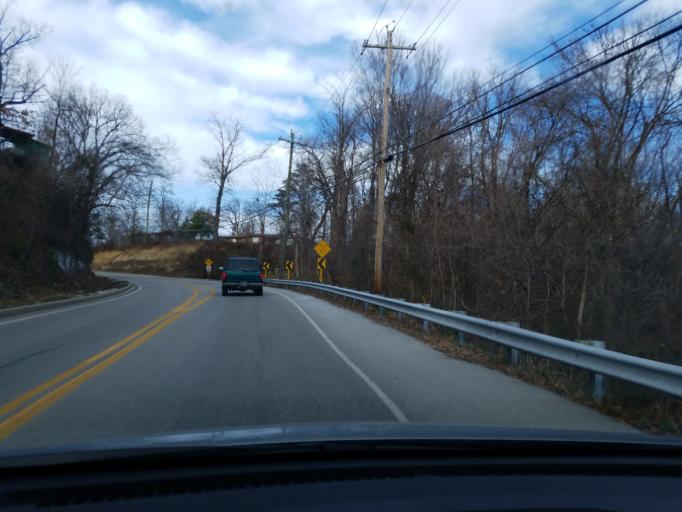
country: US
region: Indiana
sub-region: Floyd County
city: New Albany
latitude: 38.3234
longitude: -85.8573
